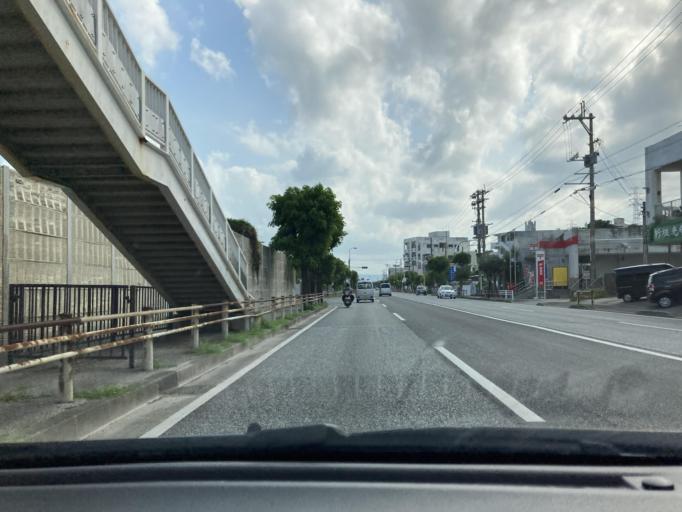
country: JP
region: Okinawa
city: Ginowan
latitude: 26.2685
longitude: 127.7910
